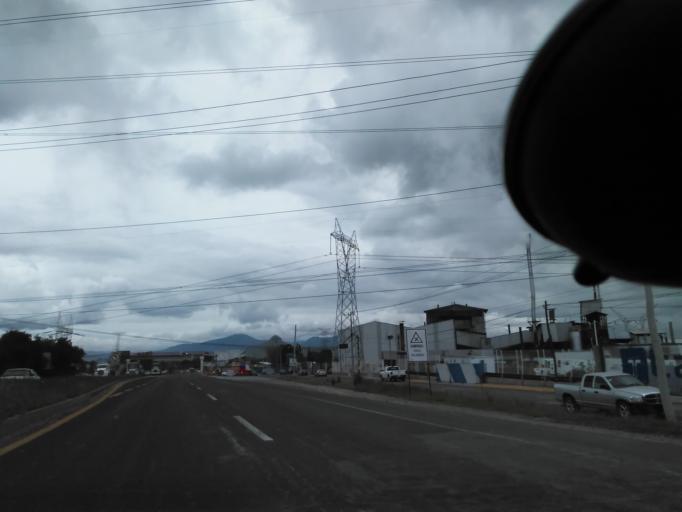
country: MX
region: Hidalgo
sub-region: Atitalaquia
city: Unidad Habitacional Antonio Osorio de Leon (Bojay)
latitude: 20.0553
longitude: -99.2672
